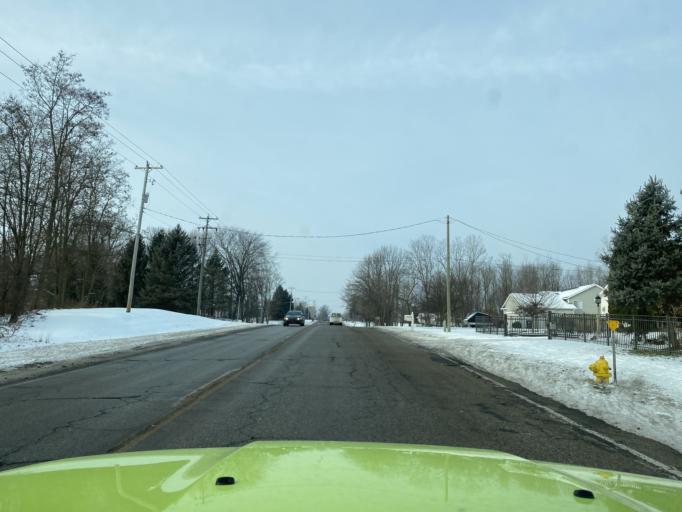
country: US
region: Michigan
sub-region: Ottawa County
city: Hudsonville
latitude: 42.8853
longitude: -85.8896
